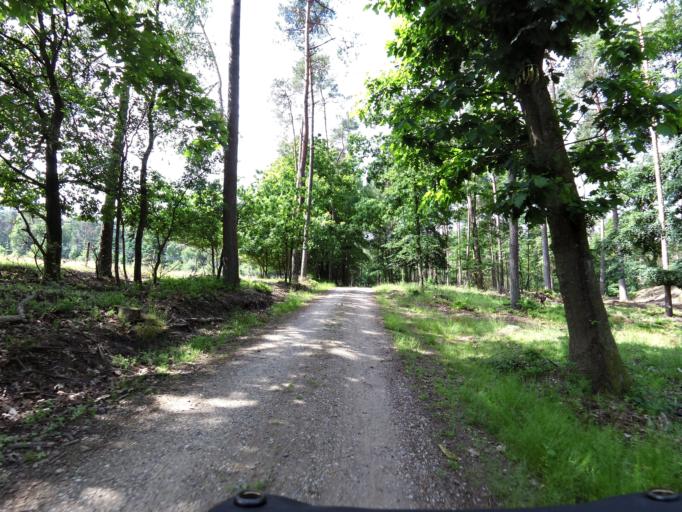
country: NL
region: Gelderland
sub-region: Gemeente Apeldoorn
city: Loenen
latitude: 52.1122
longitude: 5.9840
